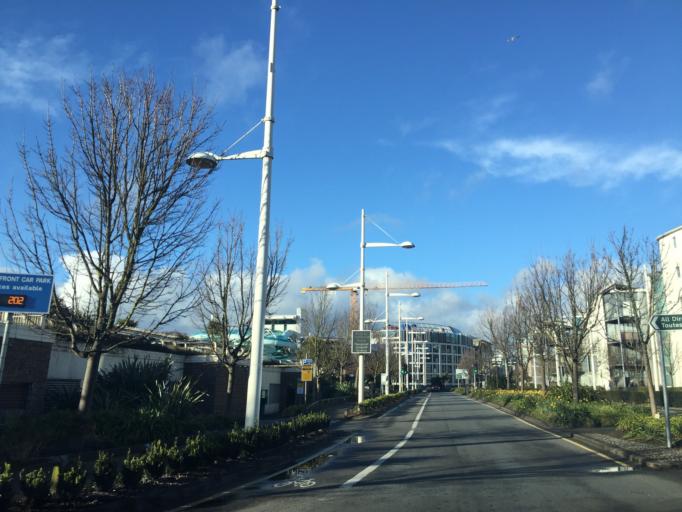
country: JE
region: St Helier
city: Saint Helier
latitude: 49.1819
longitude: -2.1137
